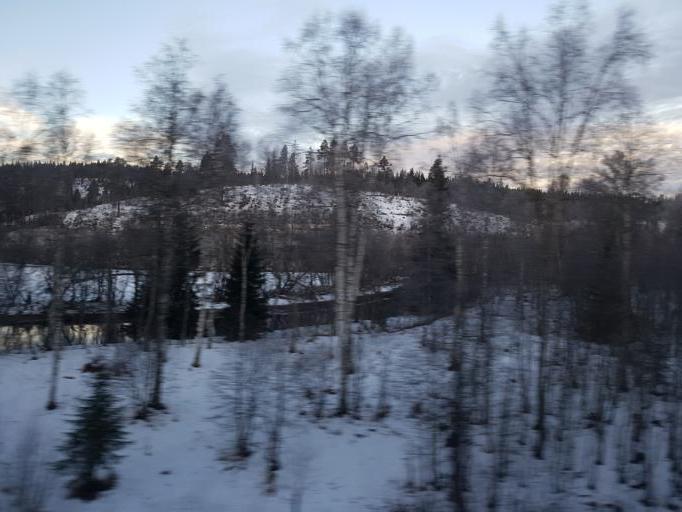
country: NO
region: Sor-Trondelag
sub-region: Rennebu
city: Berkak
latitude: 62.8797
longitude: 10.0862
